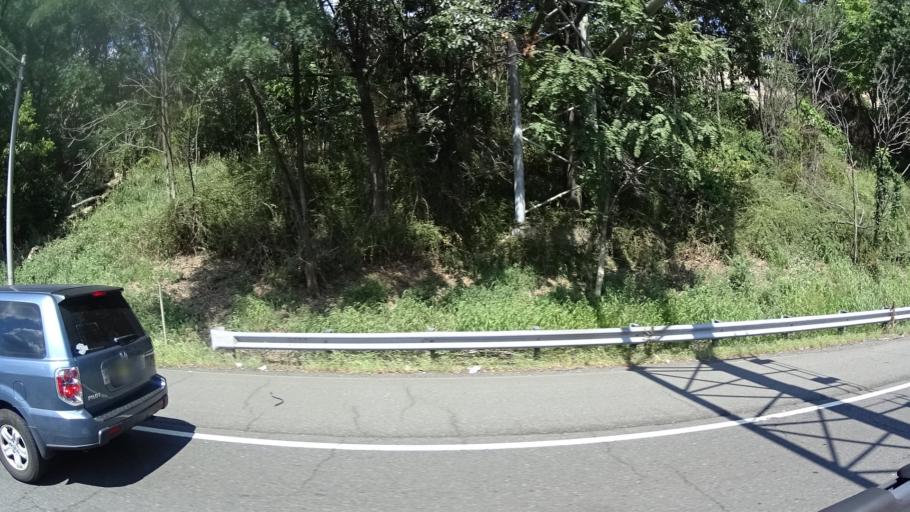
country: US
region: New Jersey
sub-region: Essex County
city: Maplewood
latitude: 40.7143
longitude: -74.2787
